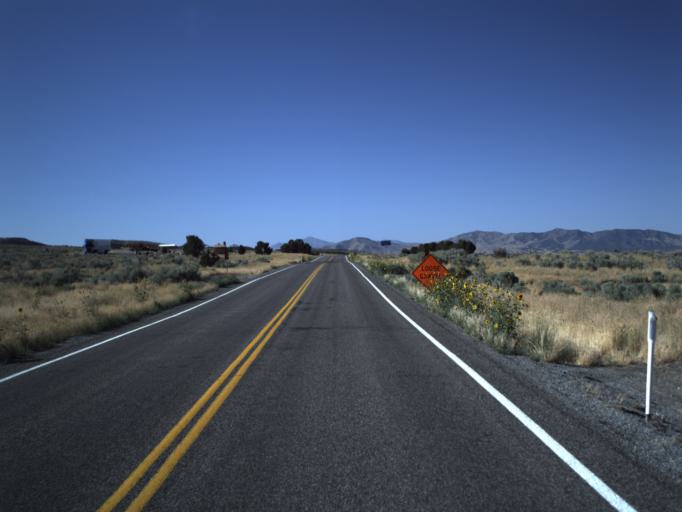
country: US
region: Utah
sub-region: Juab County
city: Mona
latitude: 39.8079
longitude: -112.1438
